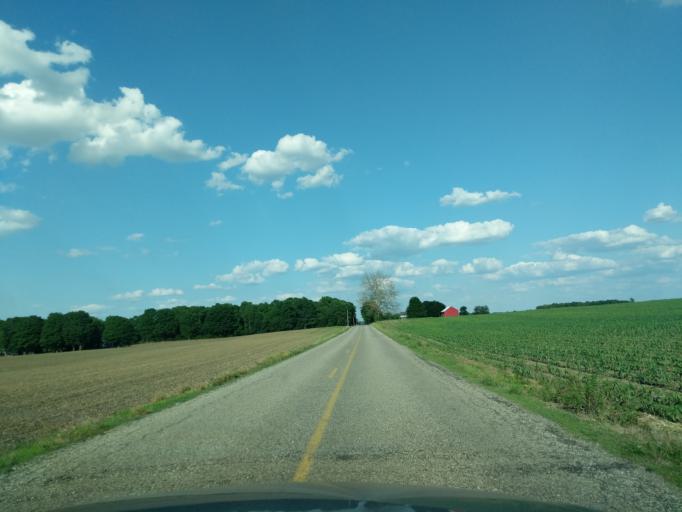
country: US
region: Indiana
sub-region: Kosciusko County
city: North Webster
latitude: 41.3024
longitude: -85.6266
